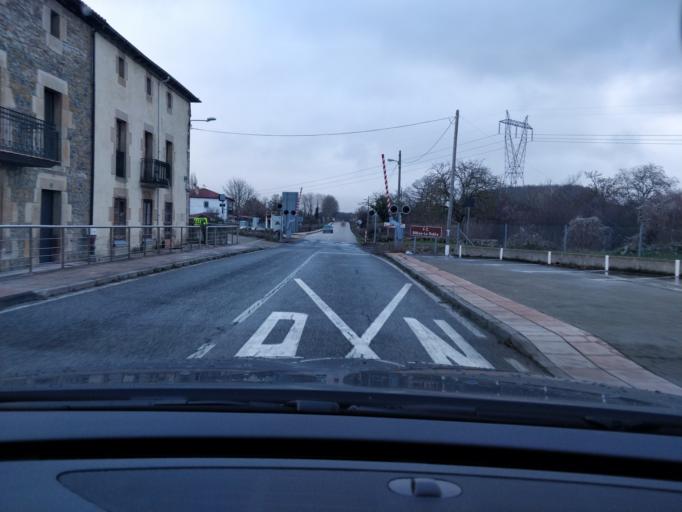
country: ES
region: Castille and Leon
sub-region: Provincia de Burgos
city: Espinosa de los Monteros
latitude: 43.0739
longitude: -3.5394
